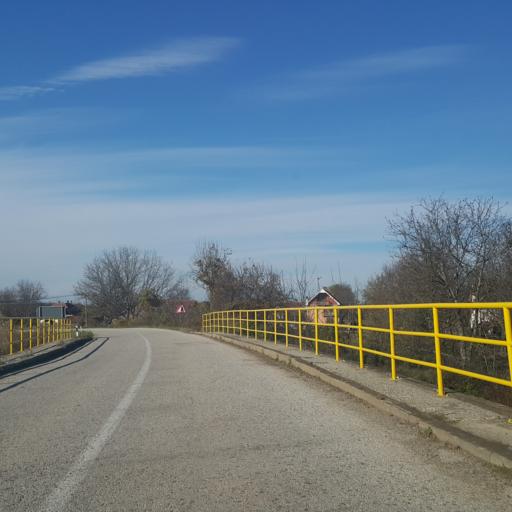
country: RS
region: Central Serbia
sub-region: Sumadijski Okrug
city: Topola
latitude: 44.2579
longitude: 20.8251
